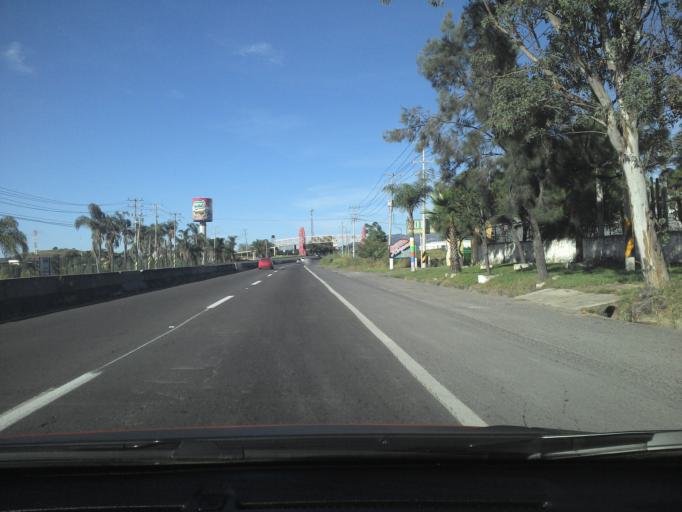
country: MX
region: Jalisco
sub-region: Tala
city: Los Ruisenores
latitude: 20.7005
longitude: -103.6887
